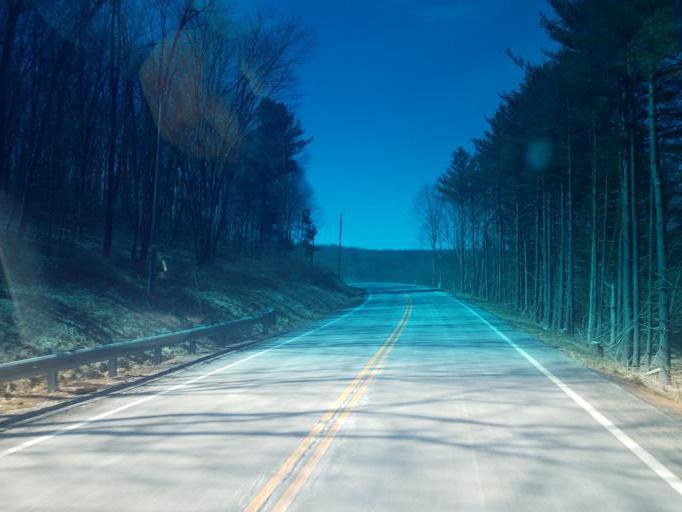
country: US
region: Ohio
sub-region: Knox County
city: Oak Hill
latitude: 40.4657
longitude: -82.1493
